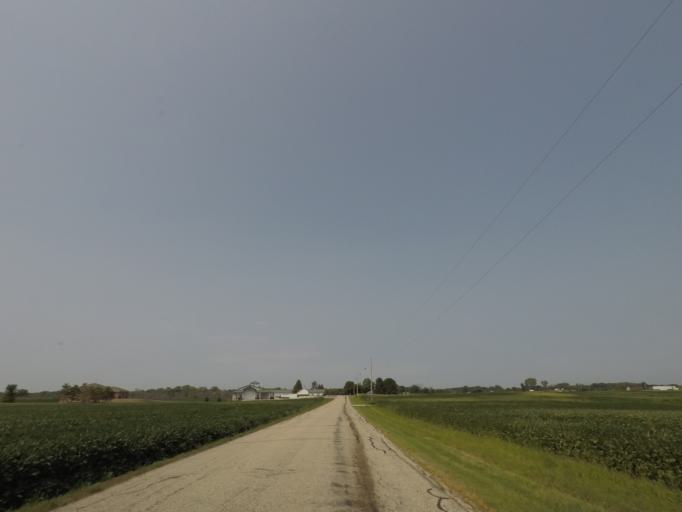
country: US
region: Wisconsin
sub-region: Waukesha County
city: Oconomowoc
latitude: 43.0654
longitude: -88.5667
